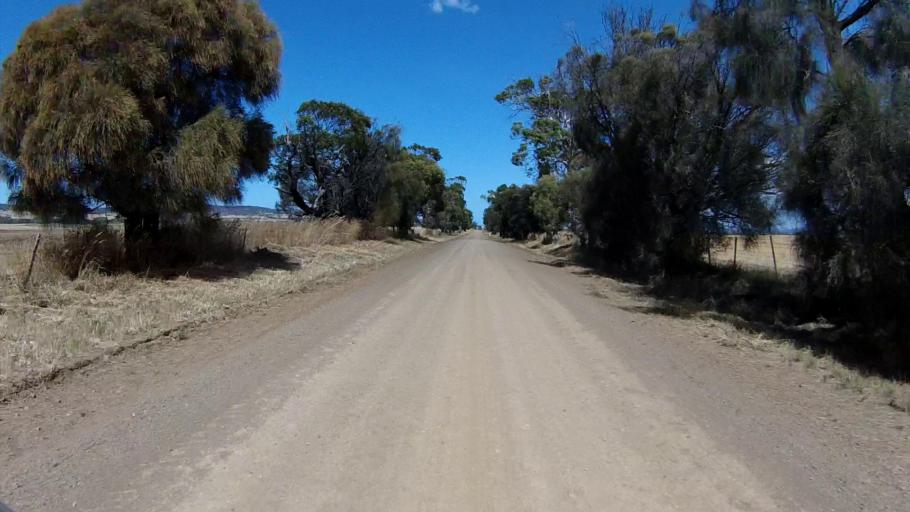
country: AU
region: Tasmania
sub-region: Break O'Day
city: St Helens
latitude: -41.9895
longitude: 148.0667
